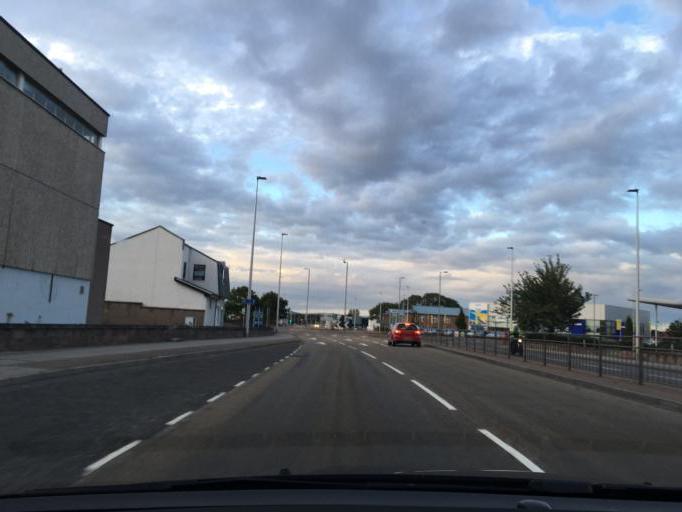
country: GB
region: Scotland
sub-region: Highland
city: Inverness
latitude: 57.4850
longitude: -4.2213
